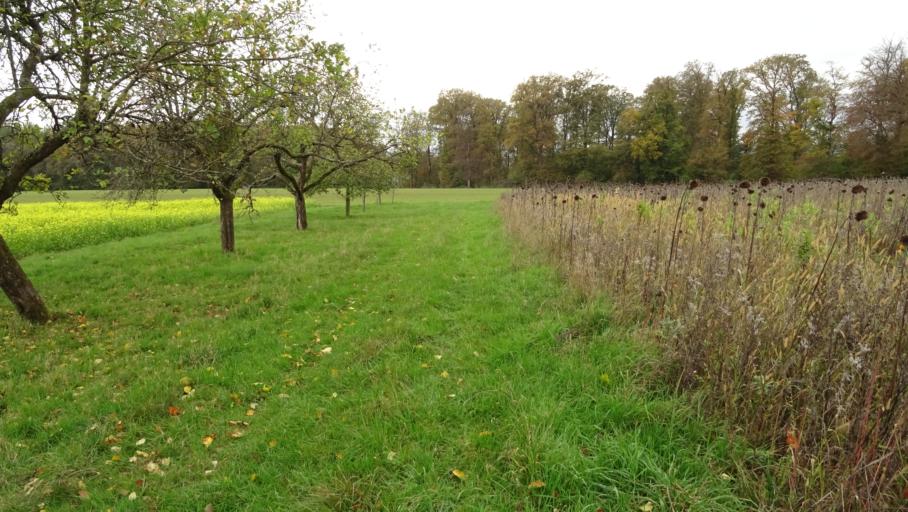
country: DE
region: Baden-Wuerttemberg
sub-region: Karlsruhe Region
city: Neckargerach
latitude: 49.3977
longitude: 9.0858
